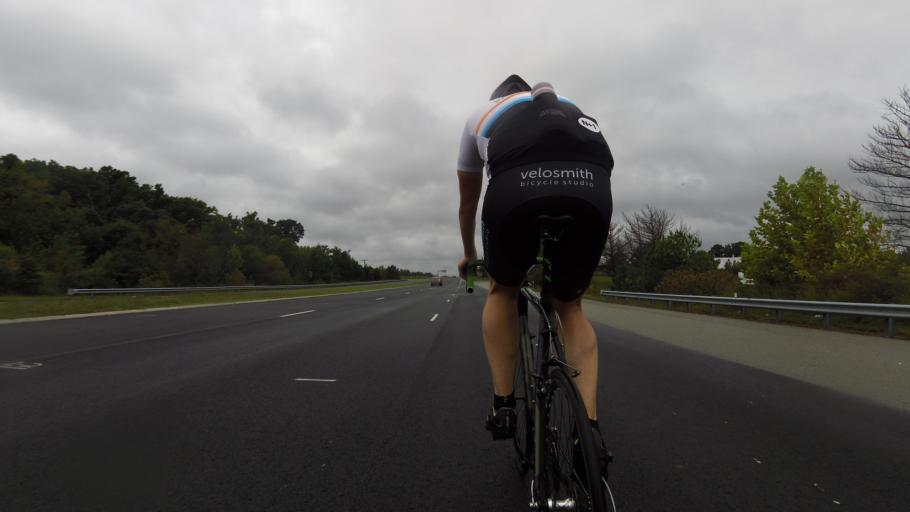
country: US
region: Virginia
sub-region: Henrico County
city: Short Pump
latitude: 37.5997
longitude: -77.6591
